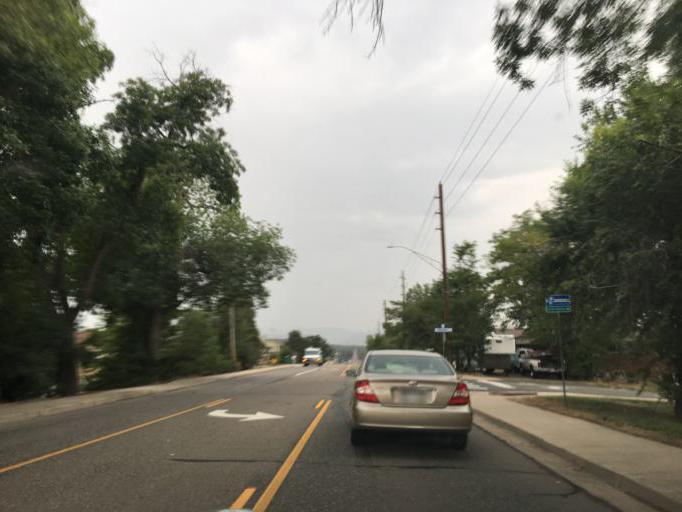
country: US
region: Colorado
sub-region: Jefferson County
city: Wheat Ridge
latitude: 39.7693
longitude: -105.1050
